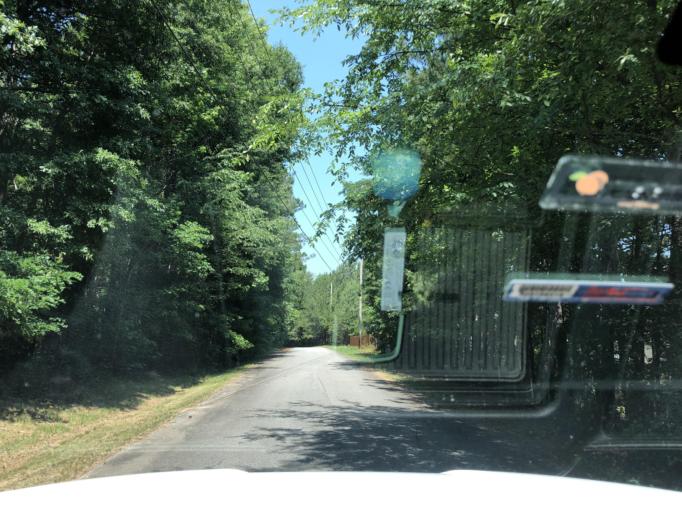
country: US
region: Georgia
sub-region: Fulton County
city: Fairburn
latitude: 33.5641
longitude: -84.5873
